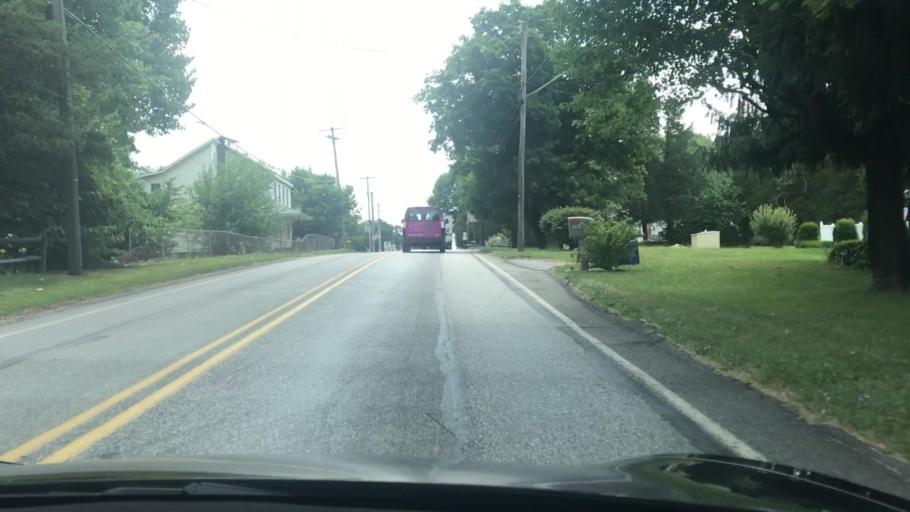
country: US
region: Pennsylvania
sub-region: York County
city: Manchester
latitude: 40.0731
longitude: -76.7661
